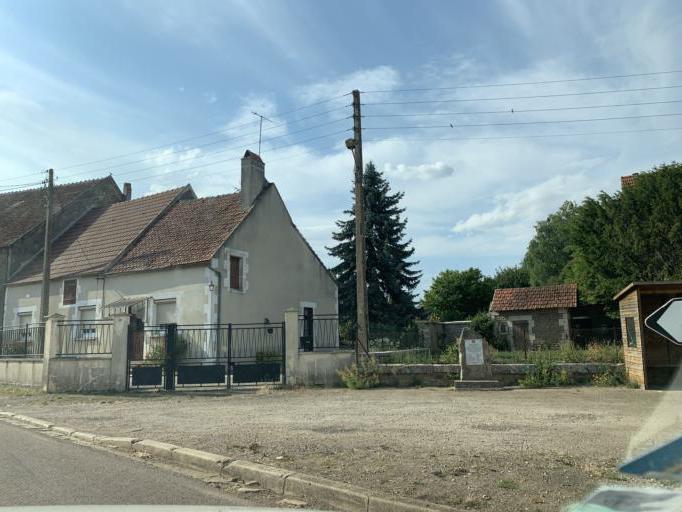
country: FR
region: Bourgogne
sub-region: Departement de l'Yonne
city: Fontenailles
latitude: 47.5202
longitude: 3.4268
